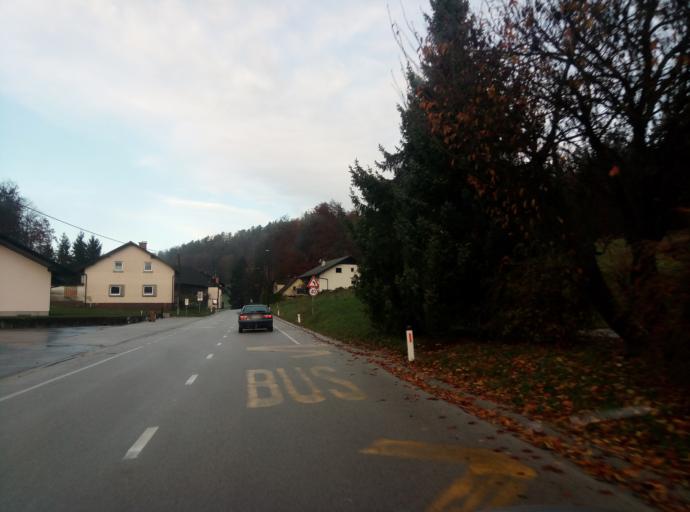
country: SI
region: Komenda
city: Moste
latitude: 46.1697
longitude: 14.5278
